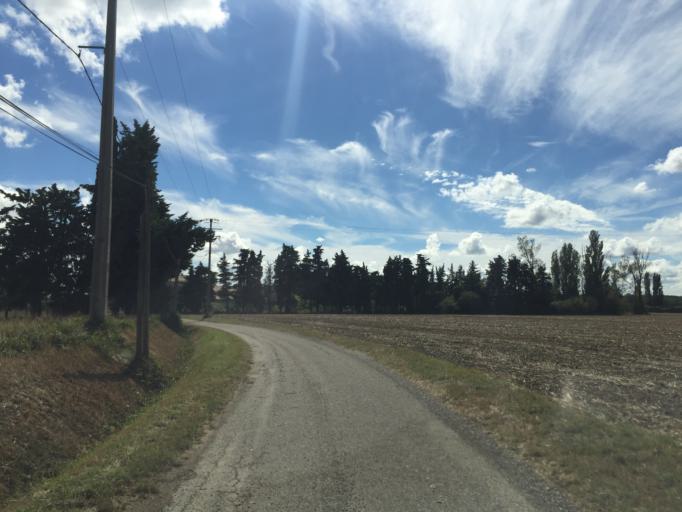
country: FR
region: Provence-Alpes-Cote d'Azur
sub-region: Departement du Vaucluse
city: Caderousse
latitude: 44.1190
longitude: 4.7365
